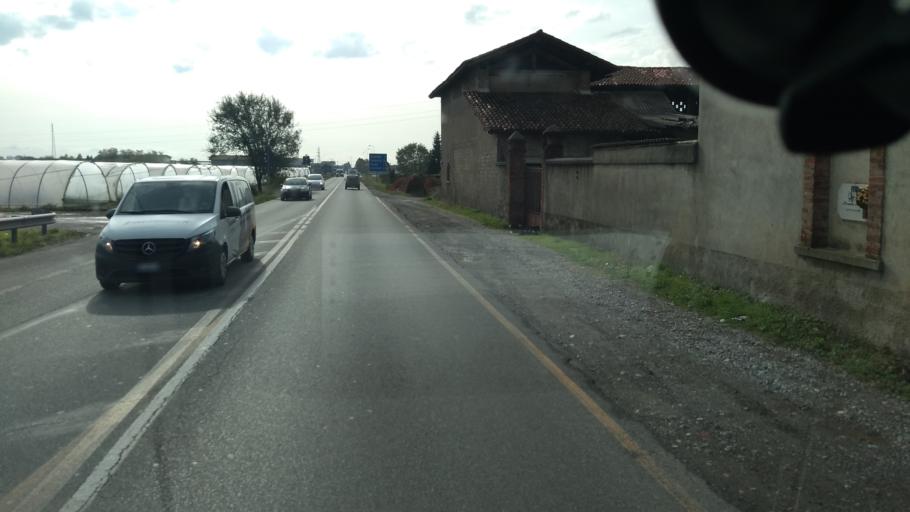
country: IT
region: Lombardy
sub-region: Provincia di Bergamo
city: Zanica
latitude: 45.6265
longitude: 9.6889
